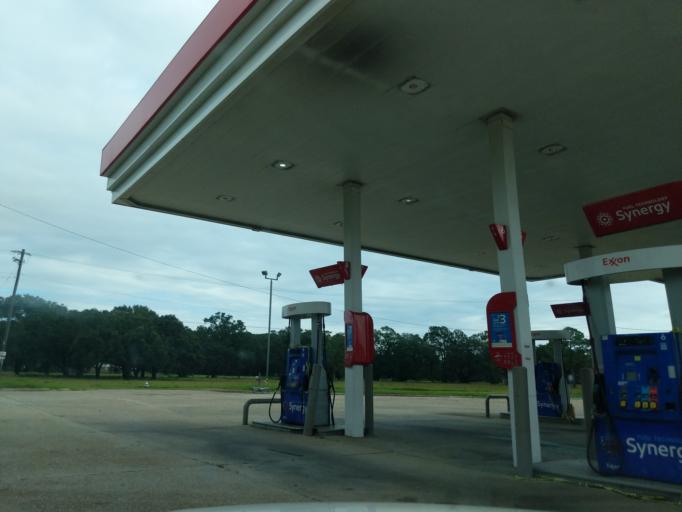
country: US
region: Alabama
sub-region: Mobile County
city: Grand Bay
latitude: 30.4997
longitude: -88.3347
